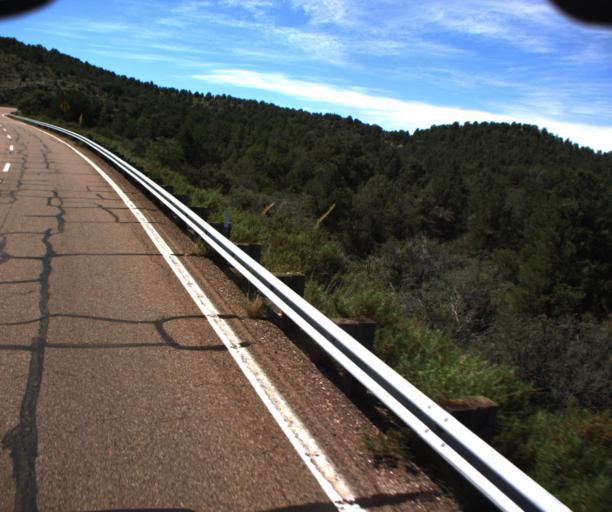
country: US
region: Arizona
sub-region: Navajo County
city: Cibecue
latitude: 33.7775
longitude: -110.5048
